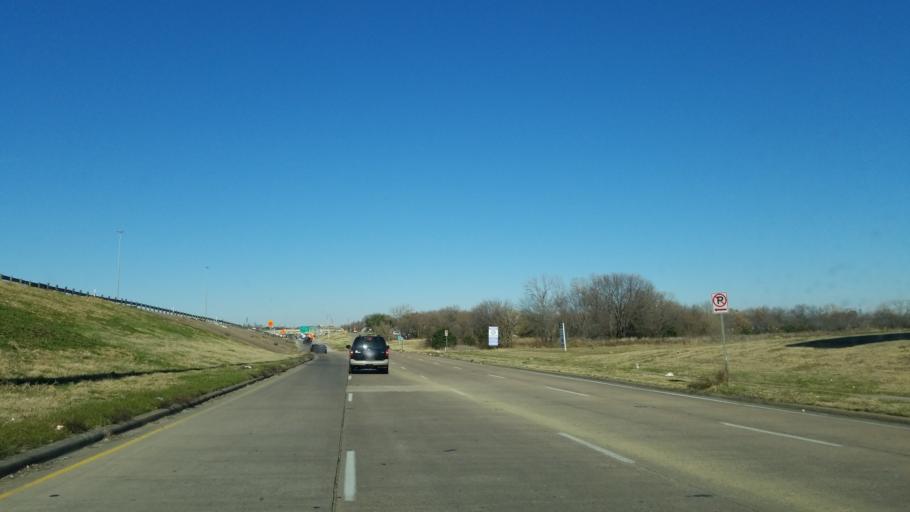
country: US
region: Texas
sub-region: Tarrant County
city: Arlington
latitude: 32.7212
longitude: -97.0620
